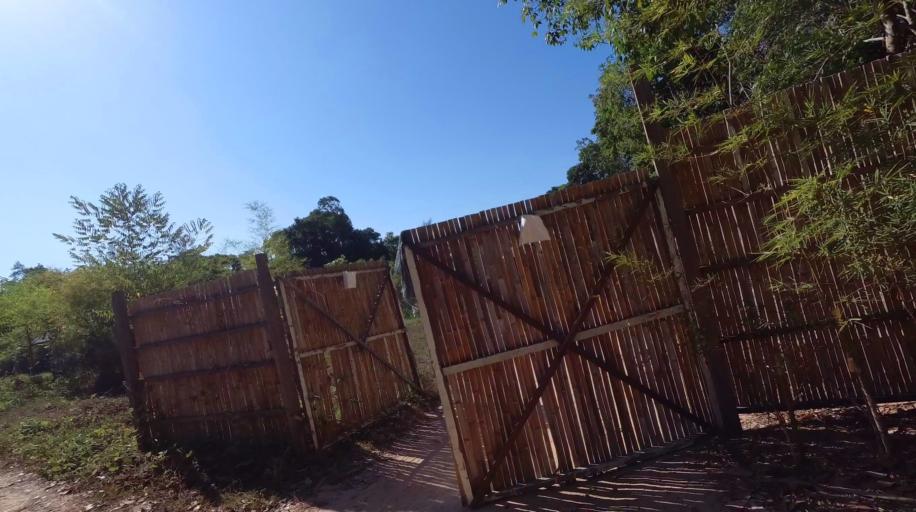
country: TH
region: Trat
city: Ko Kut
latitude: 11.6177
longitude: 102.5359
